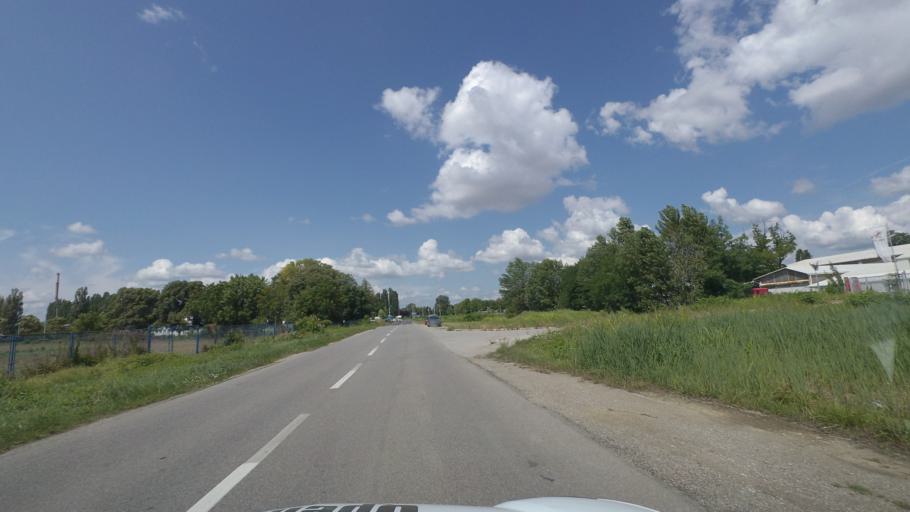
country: HR
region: Grad Zagreb
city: Dubrava
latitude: 45.7912
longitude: 16.0344
